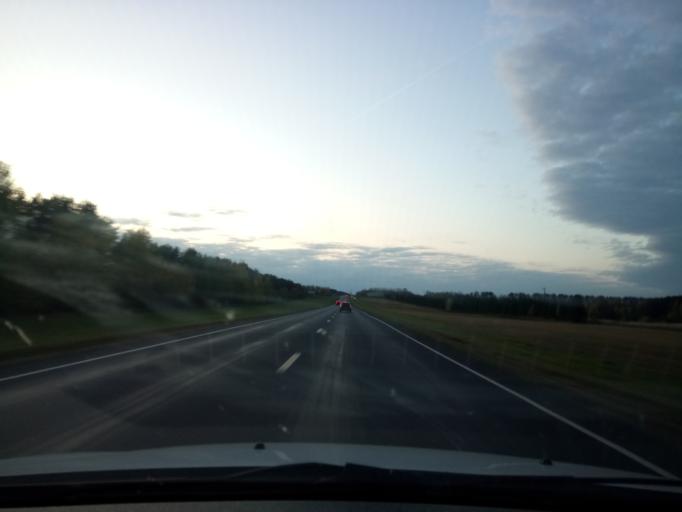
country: RU
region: Nizjnij Novgorod
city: Bol'shoye Murashkino
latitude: 55.8970
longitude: 44.7286
